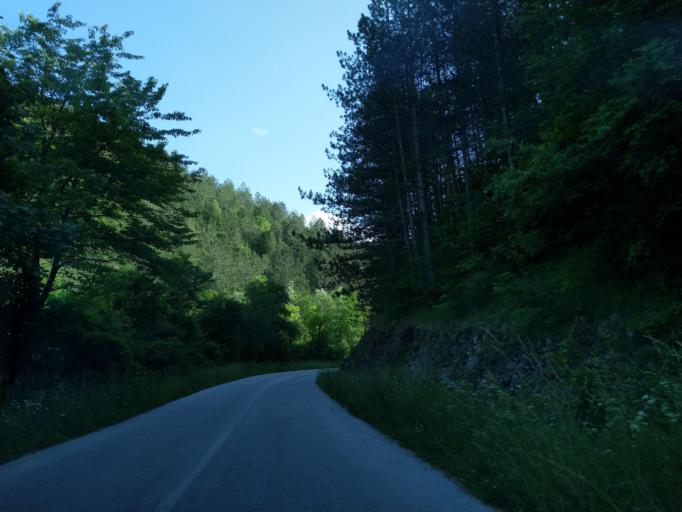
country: RS
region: Central Serbia
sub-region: Zlatiborski Okrug
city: Bajina Basta
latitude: 43.8539
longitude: 19.6229
